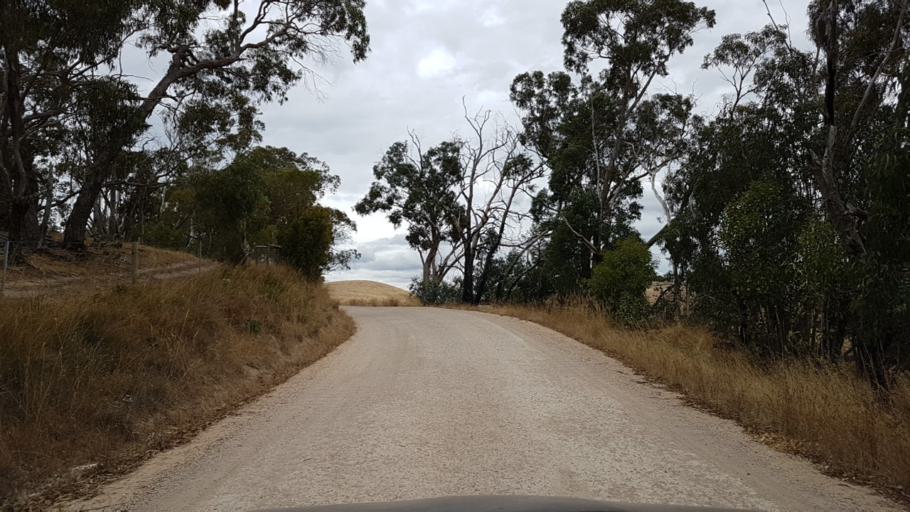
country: AU
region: South Australia
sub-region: Tea Tree Gully
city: Golden Grove
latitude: -34.8021
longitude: 138.8076
